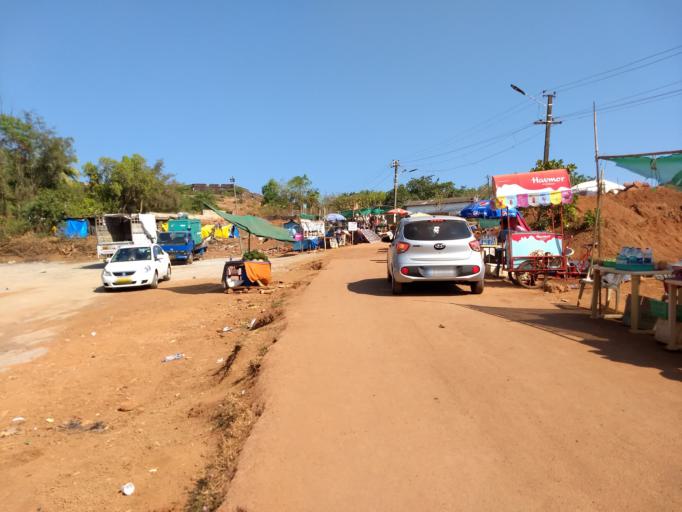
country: IN
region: Goa
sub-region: North Goa
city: Vagator
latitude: 15.6030
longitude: 73.7370
